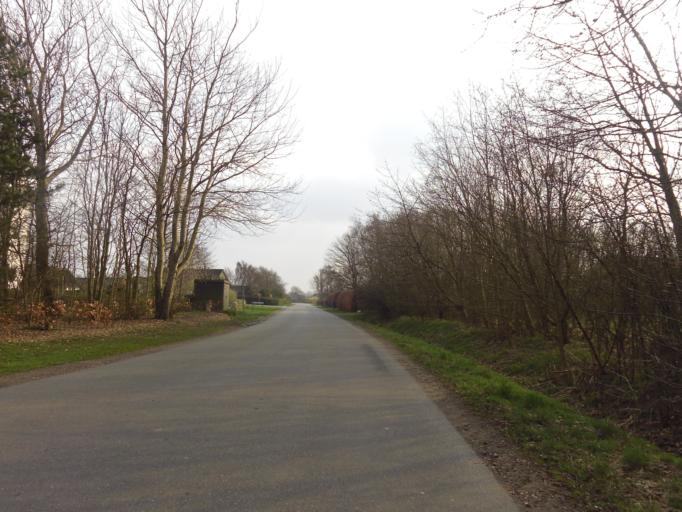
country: DK
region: South Denmark
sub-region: Esbjerg Kommune
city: Ribe
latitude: 55.3639
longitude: 8.7345
